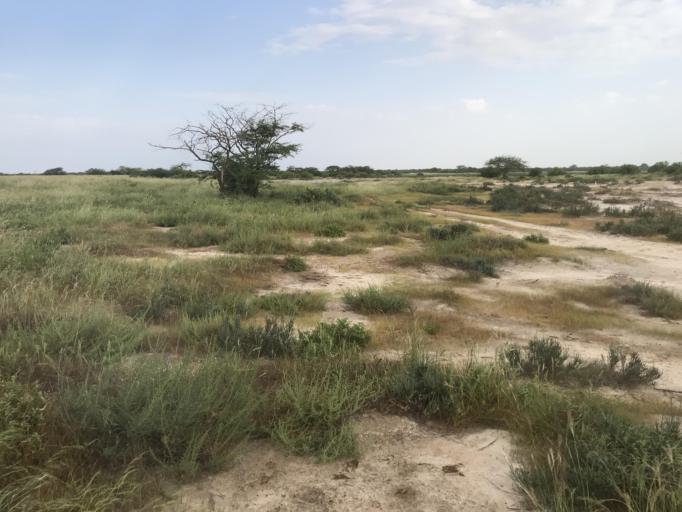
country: SN
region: Saint-Louis
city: Saint-Louis
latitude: 15.9308
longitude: -16.4634
